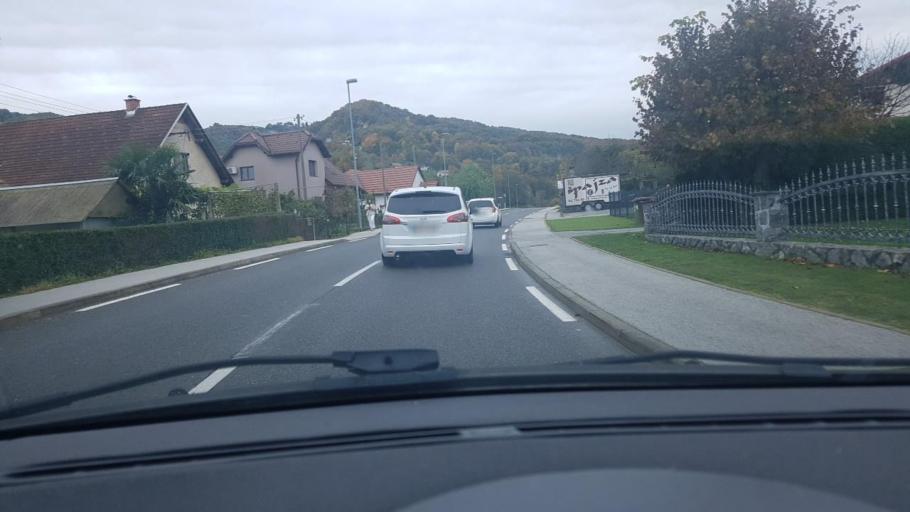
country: SI
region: Majsperk
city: Majsperk
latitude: 46.3371
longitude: 15.7368
